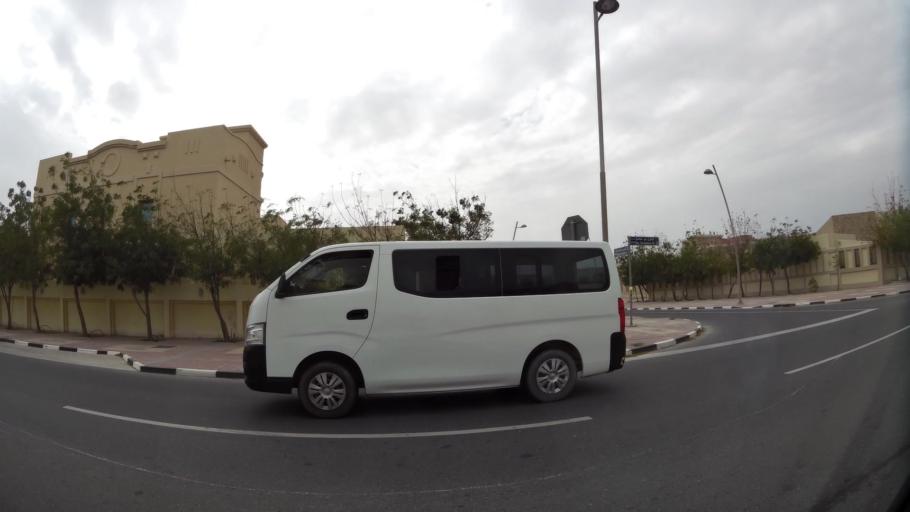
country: QA
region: Baladiyat ad Dawhah
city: Doha
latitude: 25.3365
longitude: 51.4906
